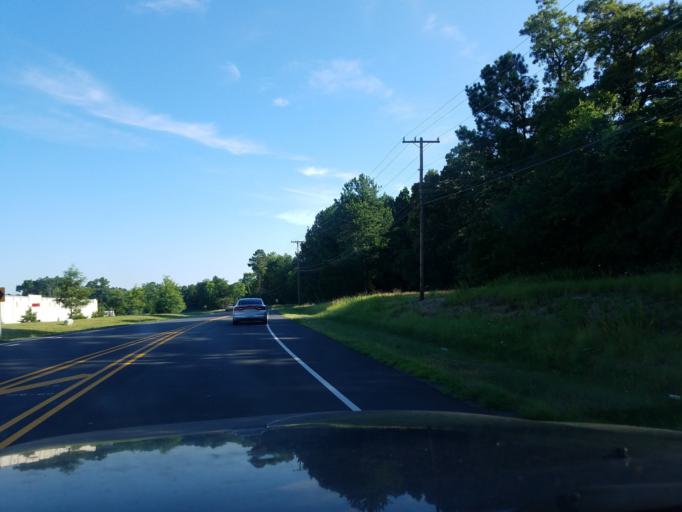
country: US
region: North Carolina
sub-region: Granville County
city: Butner
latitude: 36.1241
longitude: -78.7506
